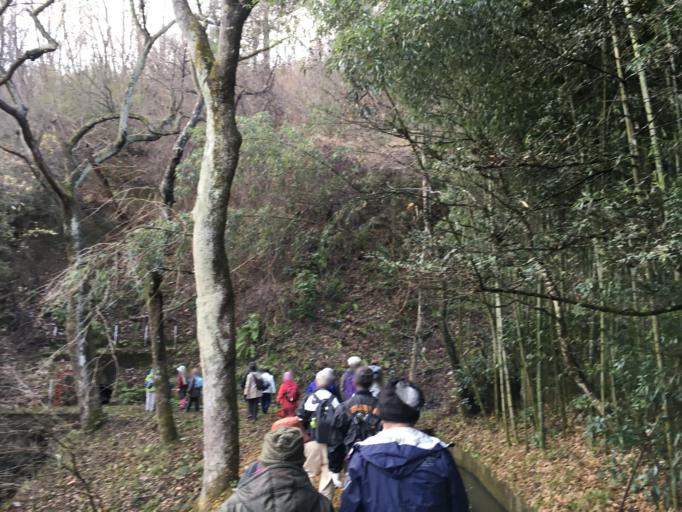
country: JP
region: Iwate
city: Ichinoseki
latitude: 38.9805
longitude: 141.1018
